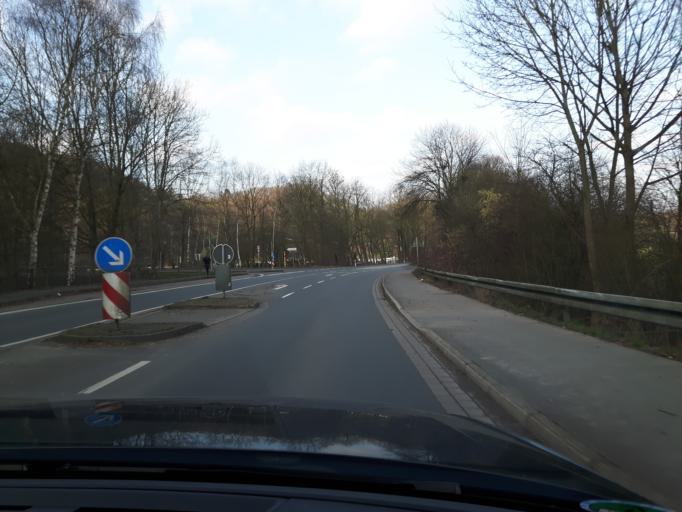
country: DE
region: North Rhine-Westphalia
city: Hattingen
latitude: 51.3902
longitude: 7.1531
